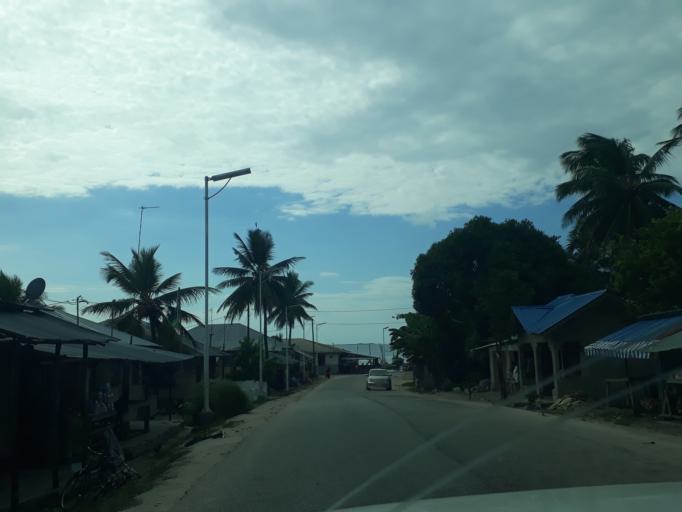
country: TZ
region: Zanzibar North
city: Mkokotoni
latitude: -5.8762
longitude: 39.2553
